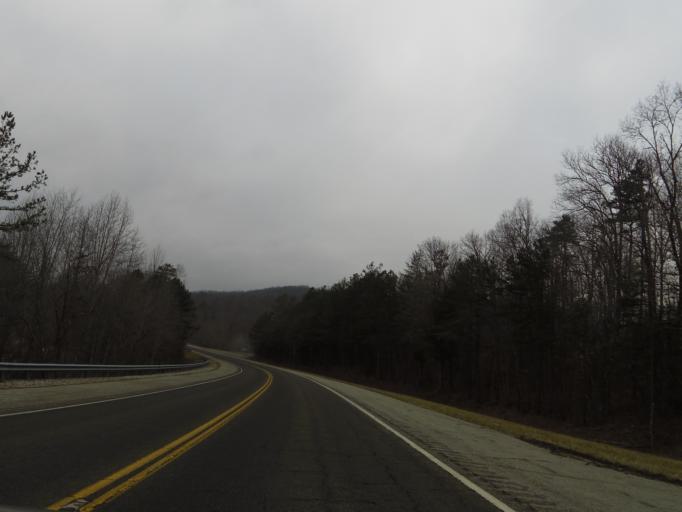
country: US
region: Tennessee
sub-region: Morgan County
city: Wartburg
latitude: 36.1258
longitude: -84.6135
